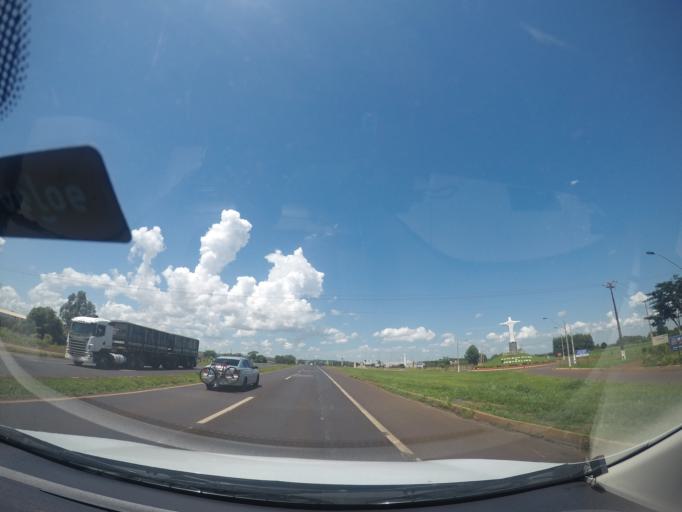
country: BR
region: Minas Gerais
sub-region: Centralina
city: Centralina
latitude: -18.5714
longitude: -49.1939
